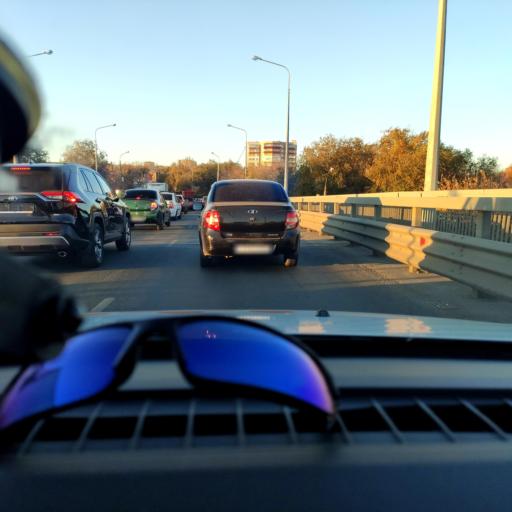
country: RU
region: Samara
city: Samara
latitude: 53.1756
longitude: 50.1936
